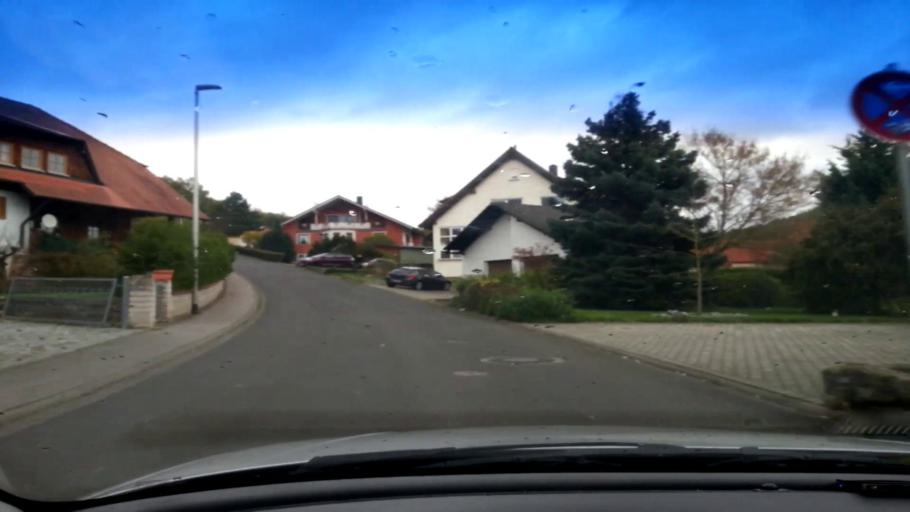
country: DE
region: Bavaria
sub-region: Regierungsbezirk Unterfranken
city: Stettfeld
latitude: 49.9731
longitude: 10.7249
